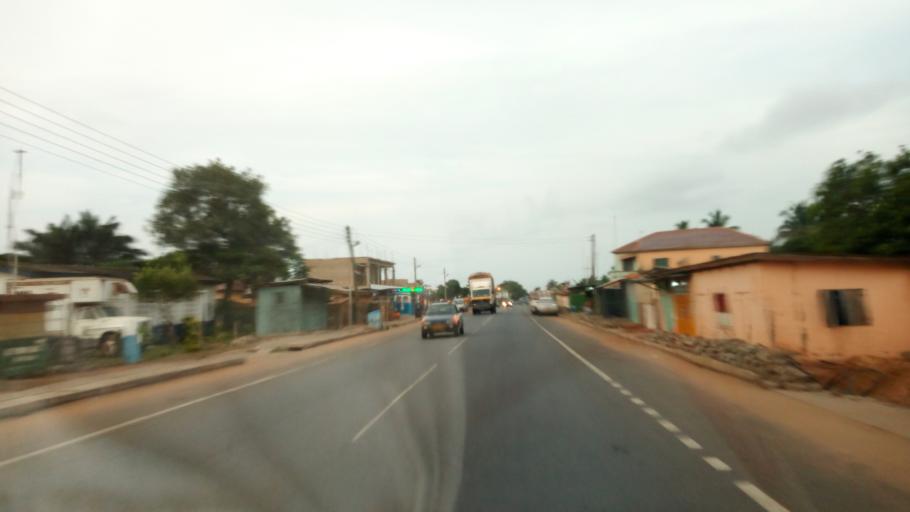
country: TG
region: Maritime
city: Lome
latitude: 6.1033
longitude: 1.1498
